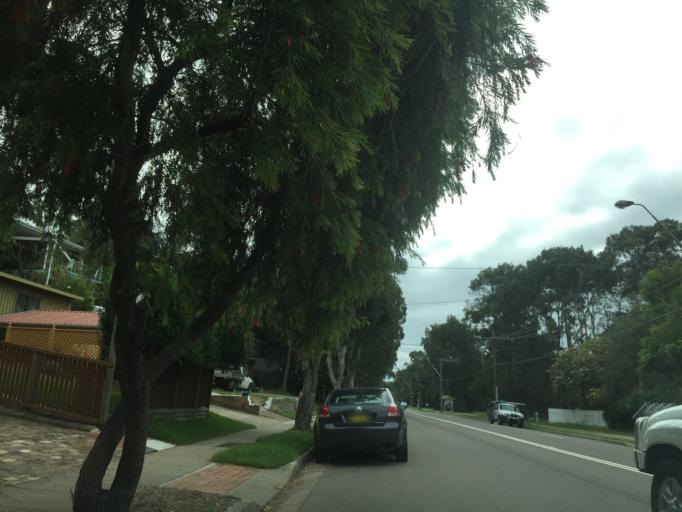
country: AU
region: New South Wales
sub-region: Pittwater
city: North Narrabeen
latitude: -33.7042
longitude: 151.2964
